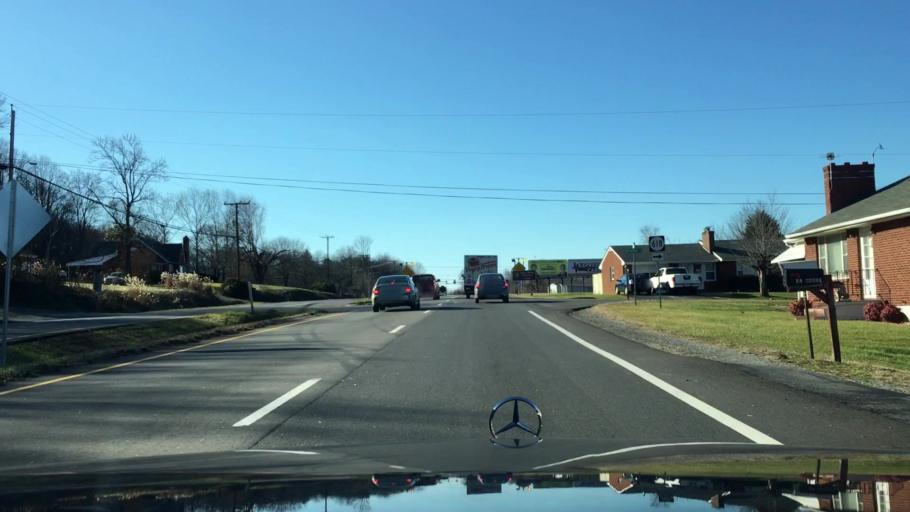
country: US
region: Virginia
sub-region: Roanoke County
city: Vinton
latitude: 37.2845
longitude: -79.8462
